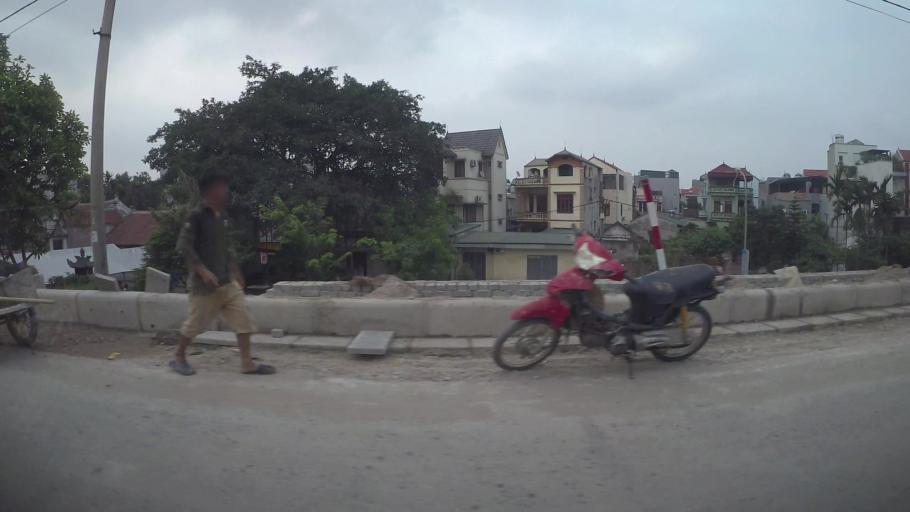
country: VN
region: Ha Noi
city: Trau Quy
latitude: 21.0214
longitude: 105.8979
